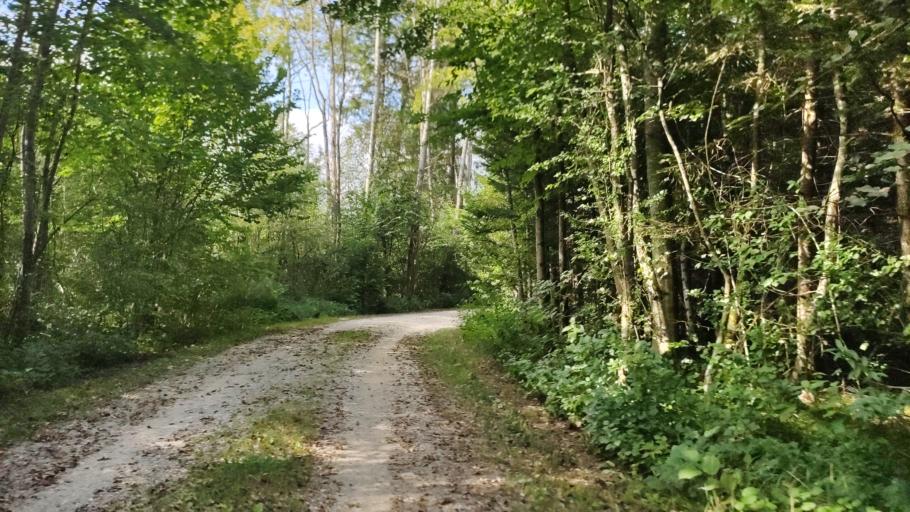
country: DE
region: Bavaria
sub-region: Upper Bavaria
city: Kaufering
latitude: 48.1207
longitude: 10.8583
